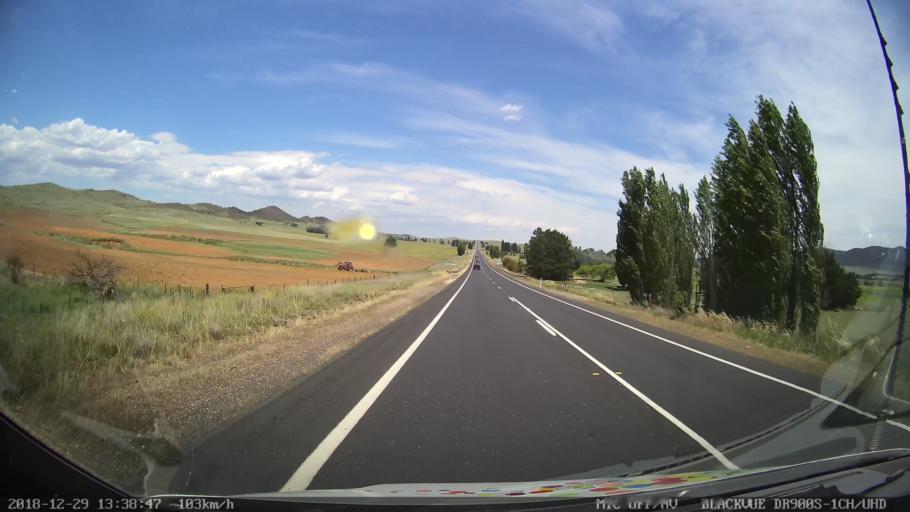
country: AU
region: New South Wales
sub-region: Cooma-Monaro
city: Cooma
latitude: -36.0032
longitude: 149.1433
